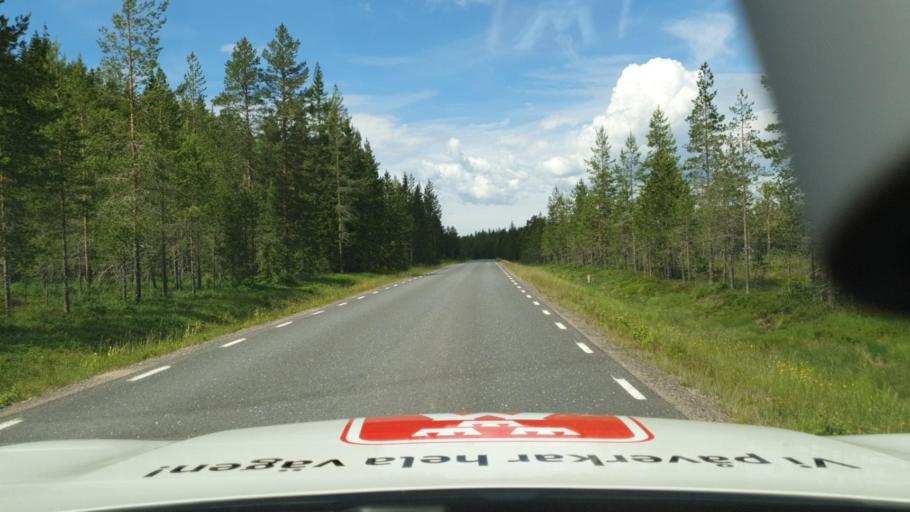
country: SE
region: Vaermland
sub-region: Torsby Kommun
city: Torsby
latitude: 60.5331
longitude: 12.8160
